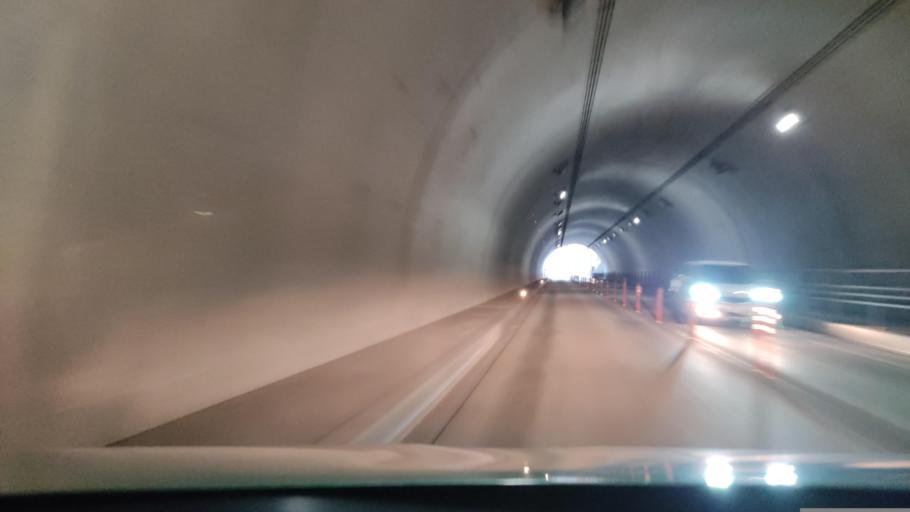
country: JP
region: Akita
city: Yokotemachi
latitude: 39.3130
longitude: 140.5834
